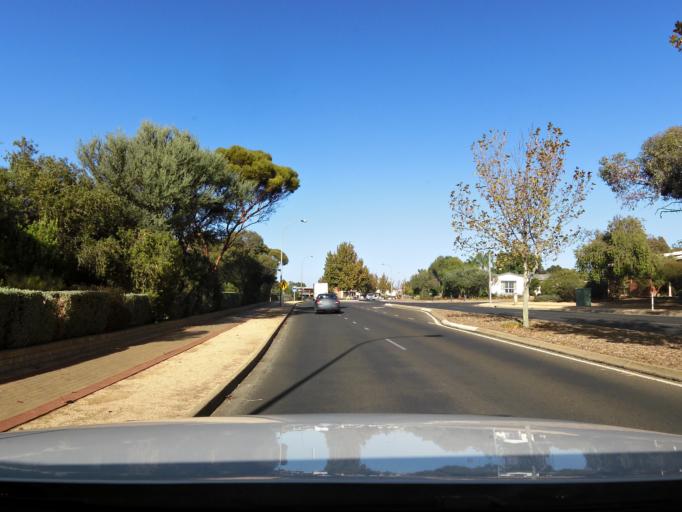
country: AU
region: South Australia
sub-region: Berri and Barmera
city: Berri
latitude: -34.2817
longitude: 140.6062
